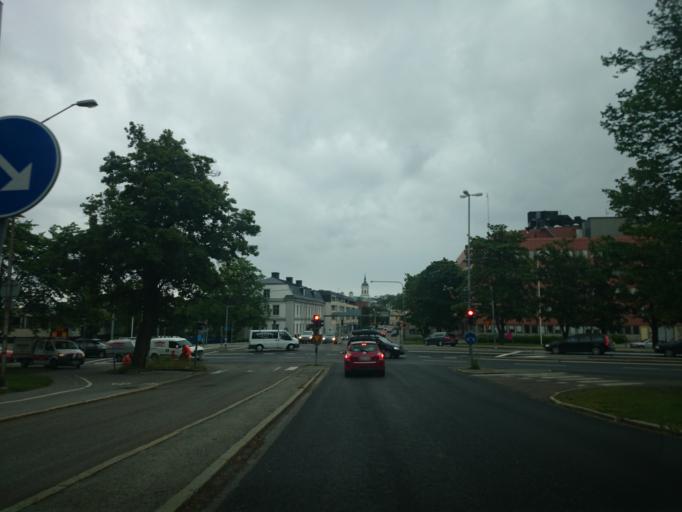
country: SE
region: Vaesternorrland
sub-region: Haernoesands Kommun
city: Haernoesand
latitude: 62.6290
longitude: 17.9309
